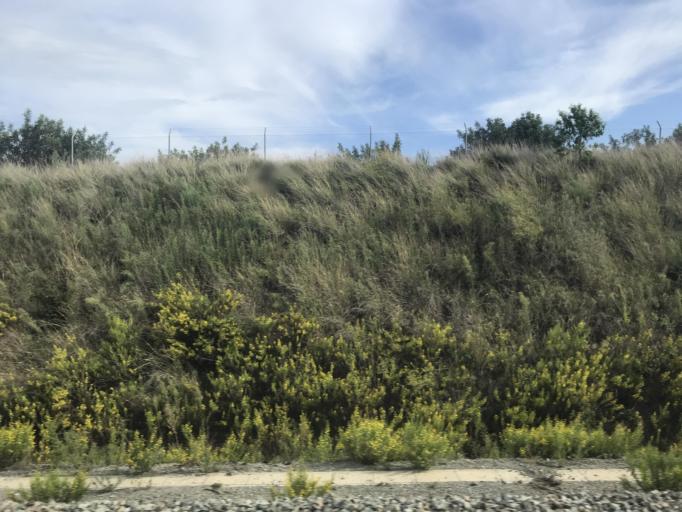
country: ES
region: Catalonia
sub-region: Provincia de Tarragona
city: Salou
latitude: 41.1021
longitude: 1.0974
